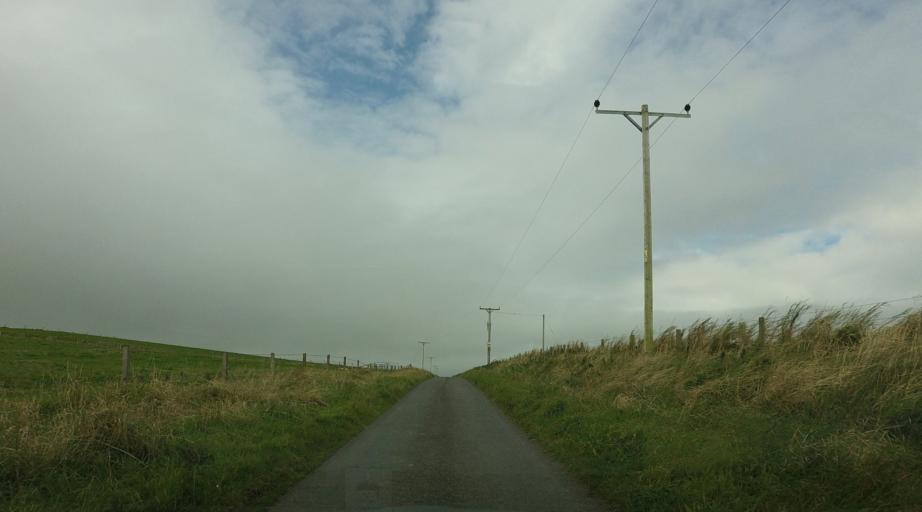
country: GB
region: Scotland
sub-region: Orkney Islands
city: Kirkwall
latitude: 58.8072
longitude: -2.9258
